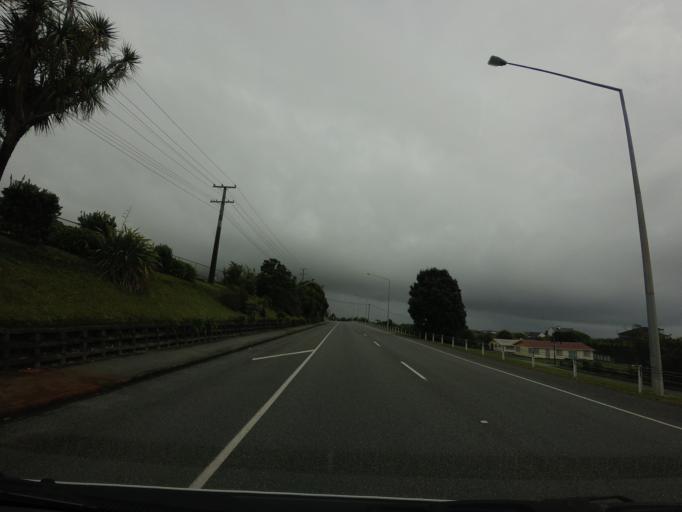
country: NZ
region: West Coast
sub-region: Grey District
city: Greymouth
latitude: -42.4751
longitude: 171.1866
